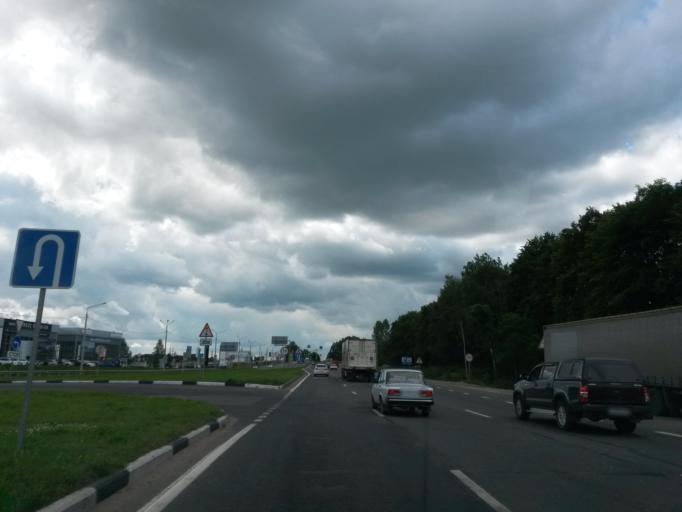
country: RU
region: Jaroslavl
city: Yaroslavl
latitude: 57.5637
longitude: 39.8277
